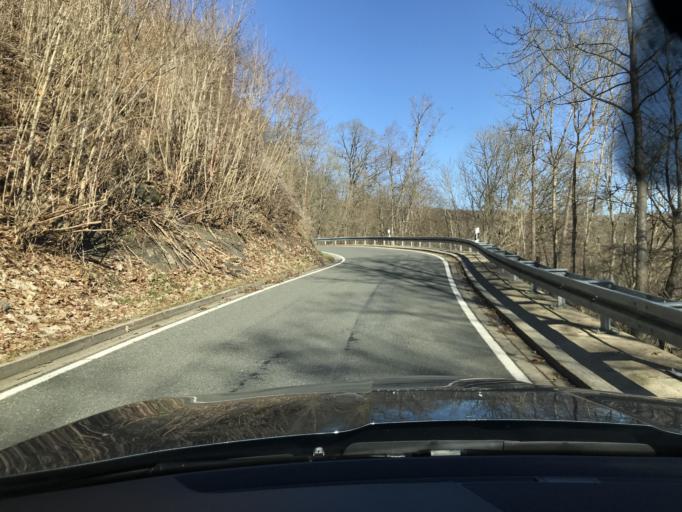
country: DE
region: Saxony-Anhalt
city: Timmenrode
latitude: 51.7238
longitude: 10.9663
